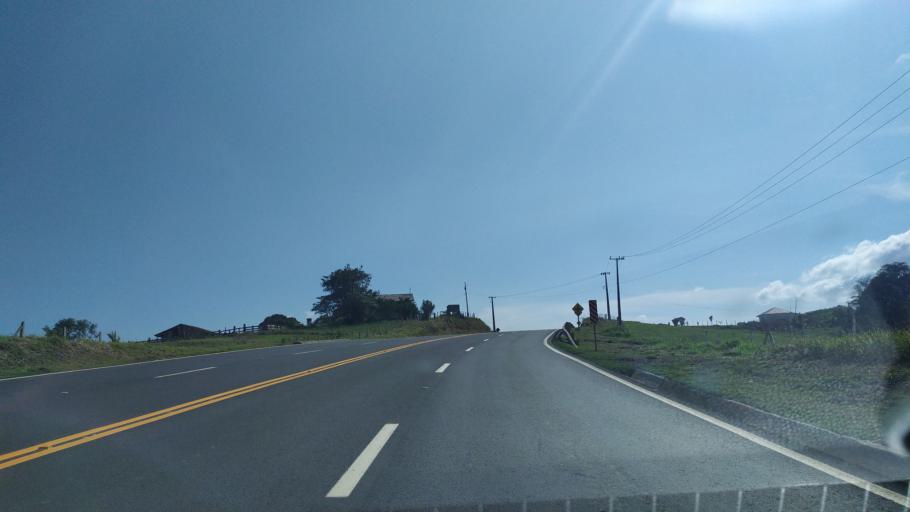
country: BR
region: Parana
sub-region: Telemaco Borba
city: Telemaco Borba
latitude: -24.2837
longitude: -50.7123
